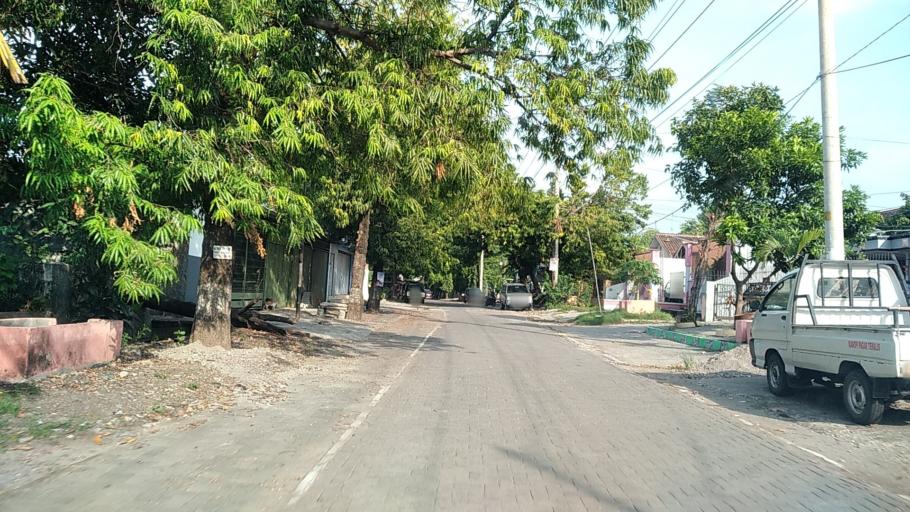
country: ID
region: Central Java
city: Semarang
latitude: -6.9872
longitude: 110.3792
